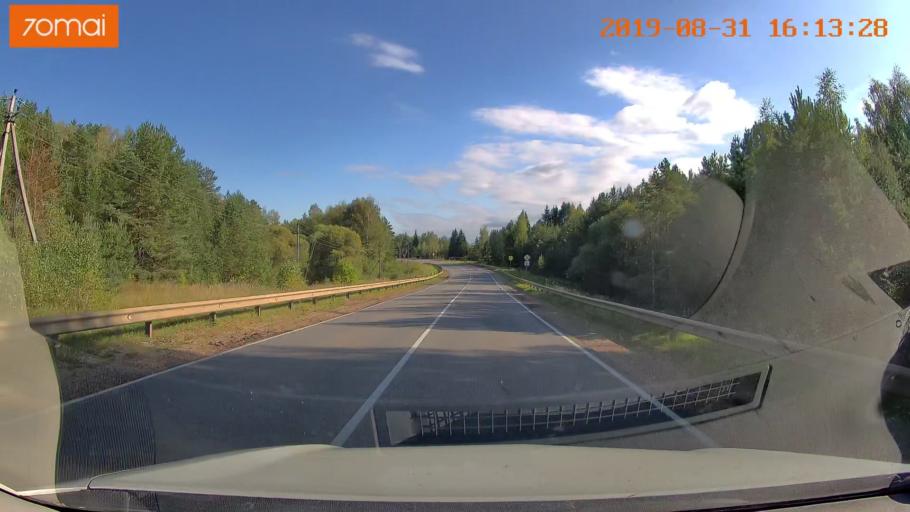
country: RU
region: Kaluga
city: Nikola-Lenivets
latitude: 54.5759
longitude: 35.4460
